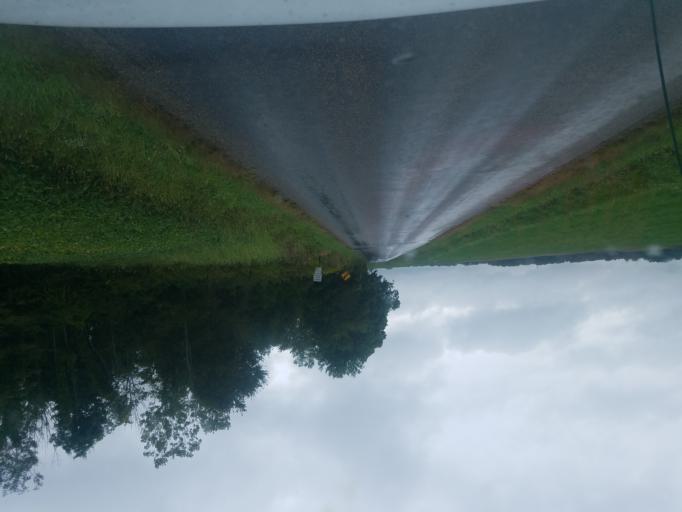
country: US
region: Ohio
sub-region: Wayne County
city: West Salem
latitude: 40.9409
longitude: -82.1277
